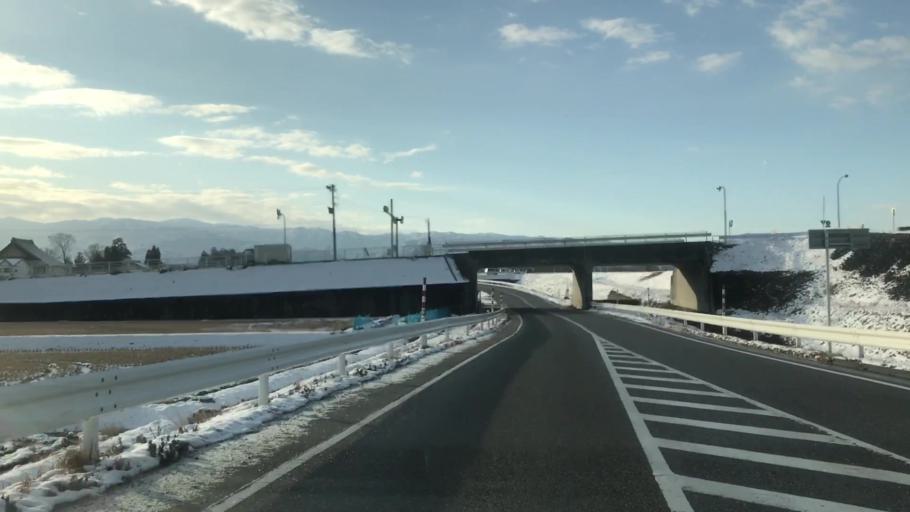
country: JP
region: Toyama
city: Toyama-shi
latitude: 36.6496
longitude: 137.2862
